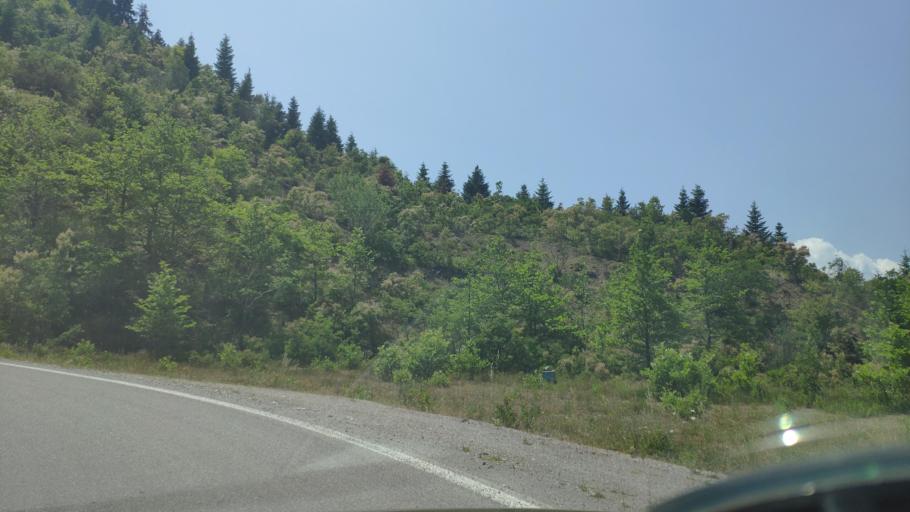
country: GR
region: Epirus
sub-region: Nomos Artas
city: Ano Kalentini
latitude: 39.2893
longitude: 21.2998
